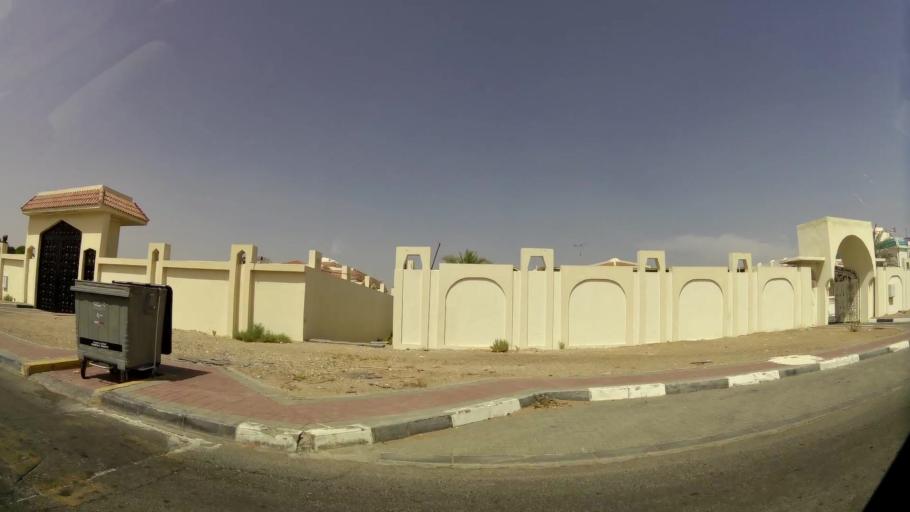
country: AE
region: Abu Dhabi
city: Al Ain
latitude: 24.2247
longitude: 55.6903
